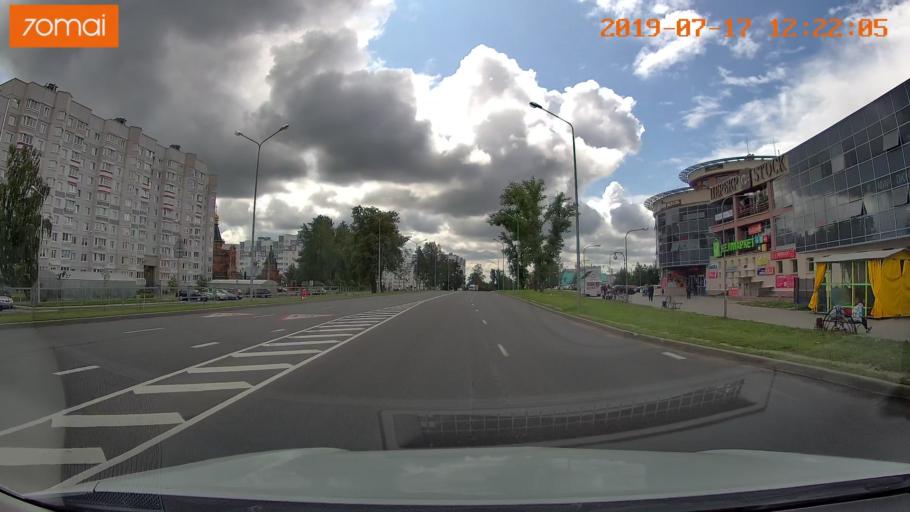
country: BY
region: Minsk
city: Borovlyany
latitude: 54.0040
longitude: 27.6778
